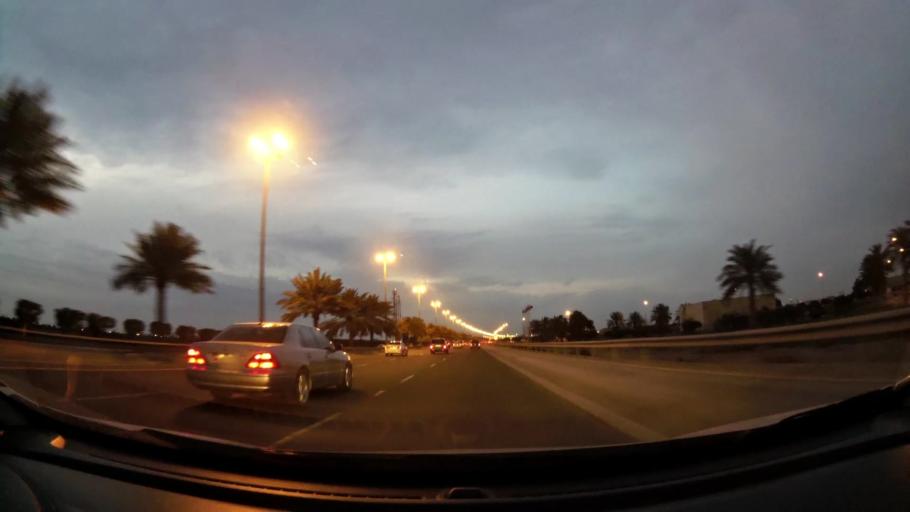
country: BH
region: Northern
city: Madinat `Isa
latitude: 26.1636
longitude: 50.5040
